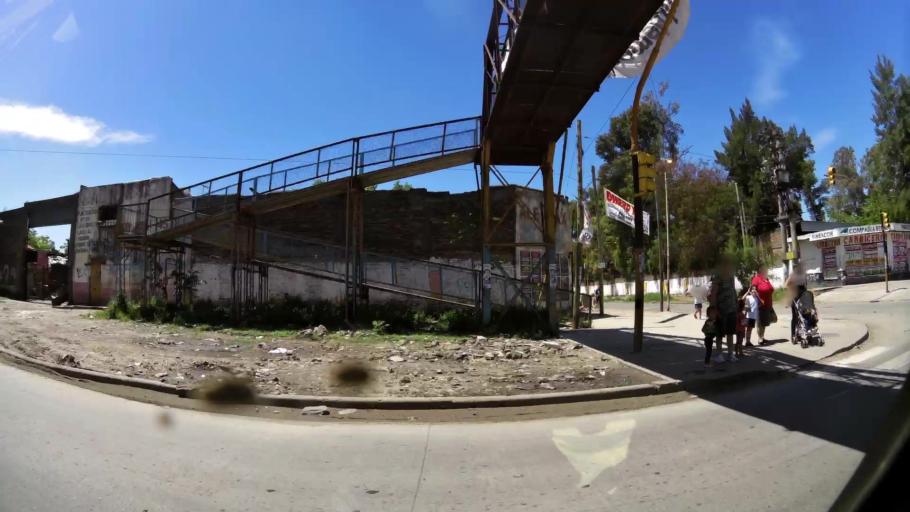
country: AR
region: Buenos Aires
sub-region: Partido de Quilmes
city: Quilmes
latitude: -34.7338
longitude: -58.3257
